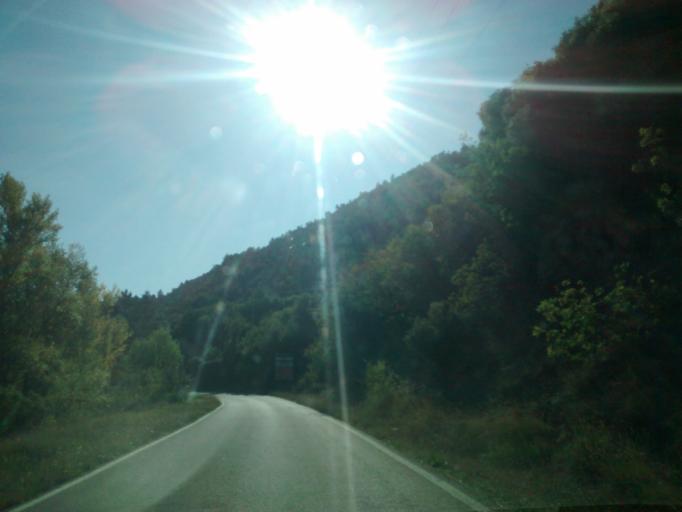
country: ES
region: Aragon
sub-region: Provincia de Huesca
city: Loarre
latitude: 42.4063
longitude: -0.6511
